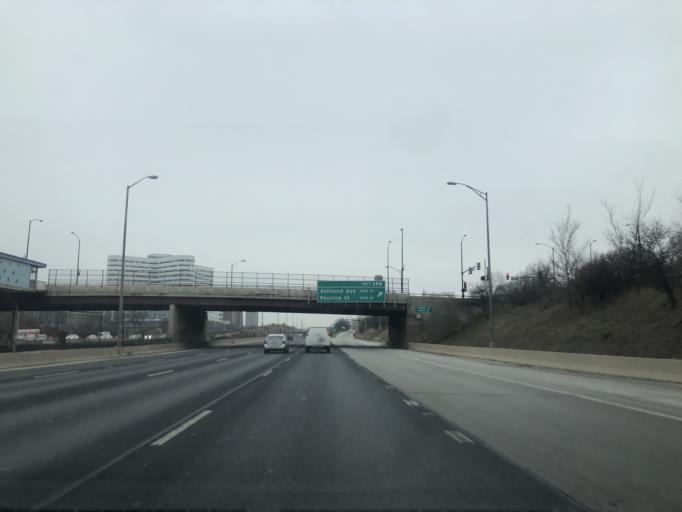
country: US
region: Illinois
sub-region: Cook County
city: Chicago
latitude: 41.8762
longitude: -87.6608
